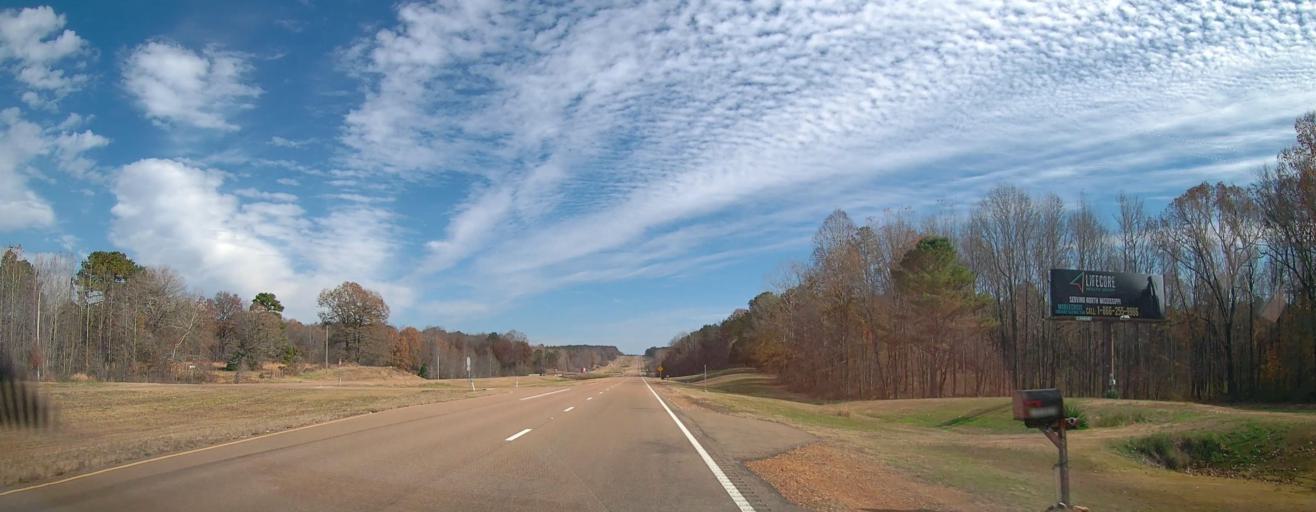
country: US
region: Mississippi
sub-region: Benton County
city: Ashland
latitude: 34.9515
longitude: -89.0662
